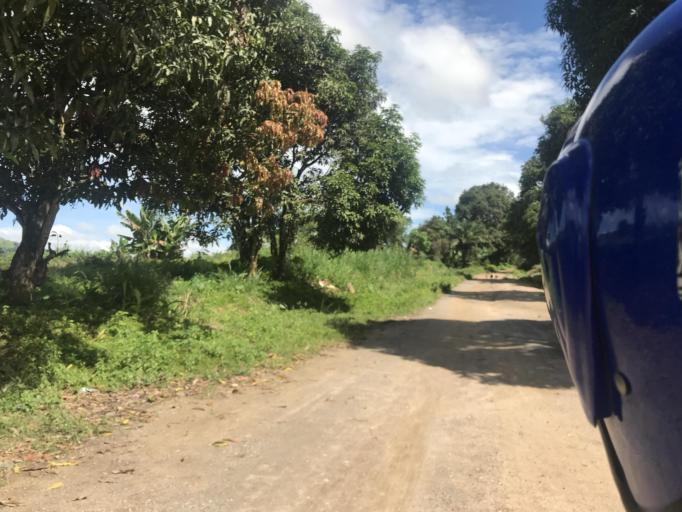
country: SL
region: Eastern Province
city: Koidu
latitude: 8.6404
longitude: -10.9879
